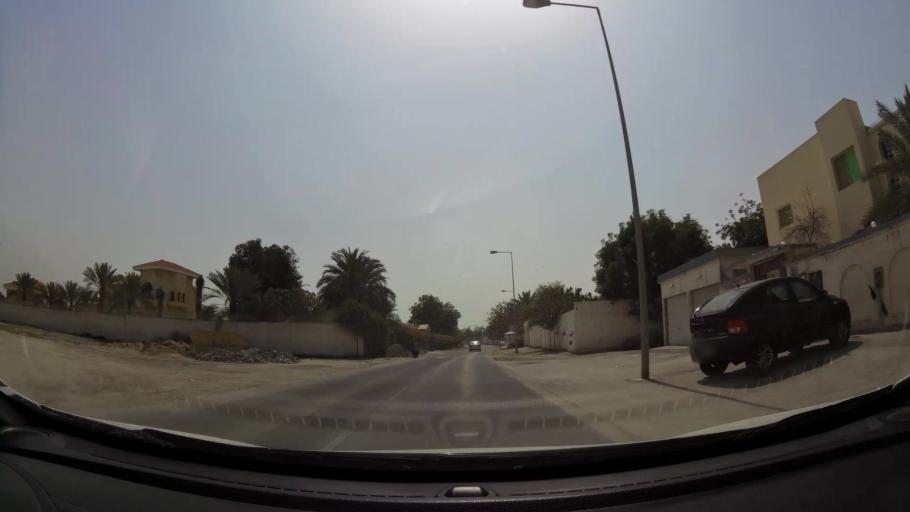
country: BH
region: Manama
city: Jidd Hafs
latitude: 26.2233
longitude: 50.4835
